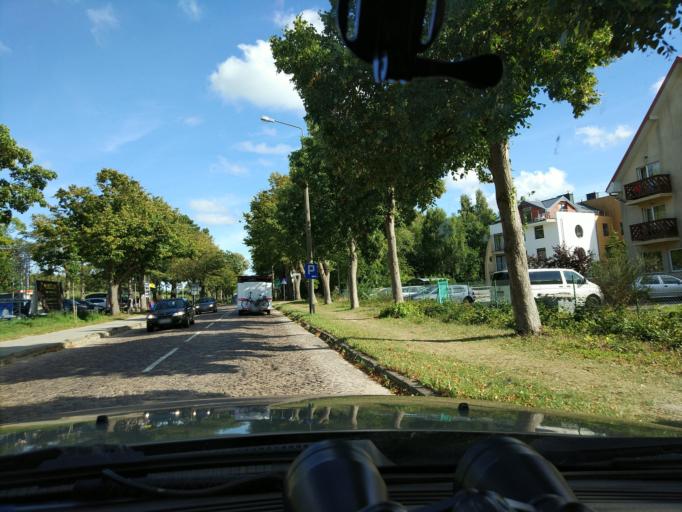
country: PL
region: Pomeranian Voivodeship
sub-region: Powiat pucki
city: Jastrzebia Gora
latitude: 54.8298
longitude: 18.3306
